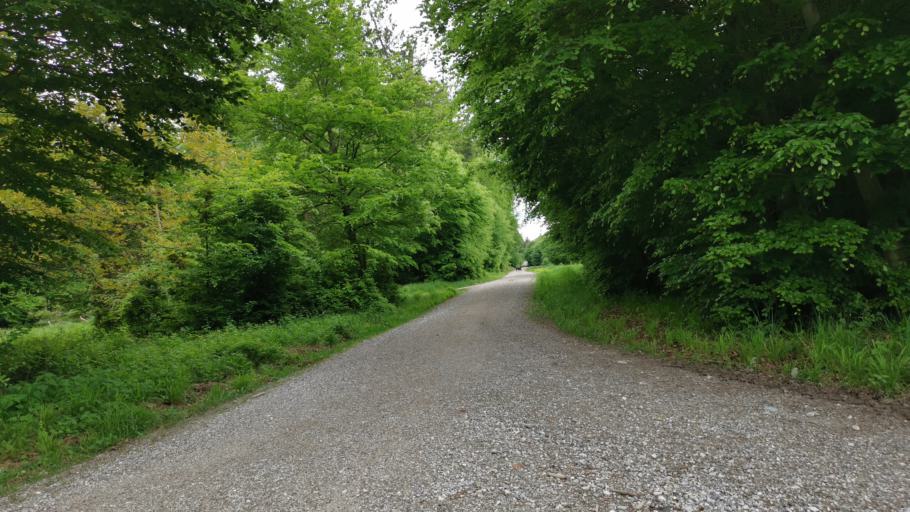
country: DE
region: Bavaria
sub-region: Upper Bavaria
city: Baierbrunn
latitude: 48.0240
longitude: 11.4607
